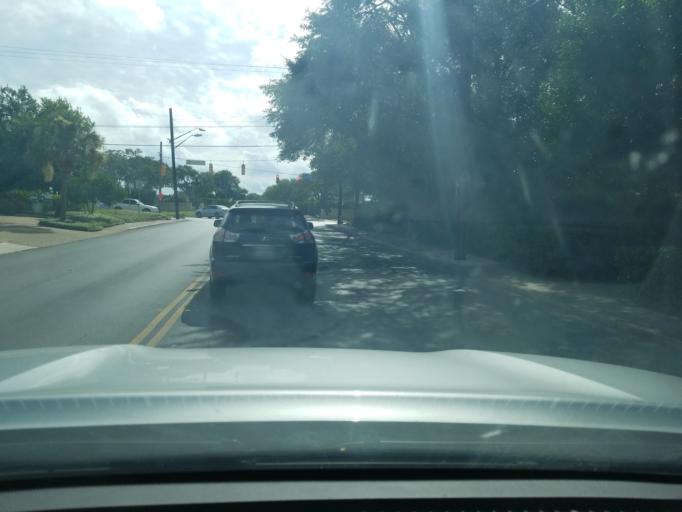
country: US
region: Texas
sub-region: Bexar County
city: Terrell Hills
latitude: 29.4657
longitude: -98.4615
